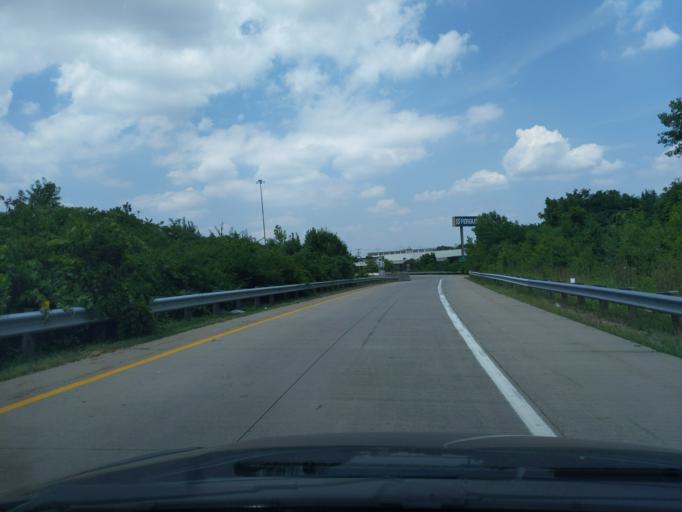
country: US
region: Ohio
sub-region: Hamilton County
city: Sharonville
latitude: 39.2872
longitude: -84.4266
